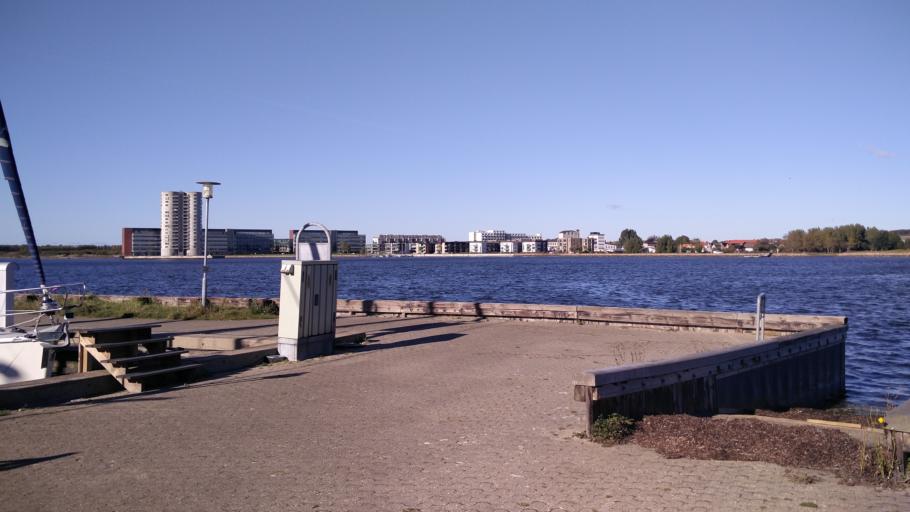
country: DK
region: North Denmark
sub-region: Alborg Kommune
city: Aalborg
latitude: 57.0581
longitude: 9.9042
